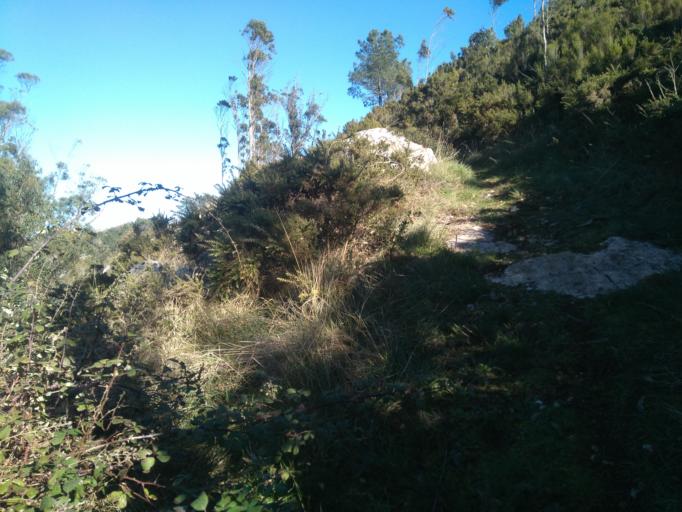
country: PT
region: Leiria
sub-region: Porto de Mos
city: Porto de Mos
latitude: 39.5361
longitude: -8.8514
